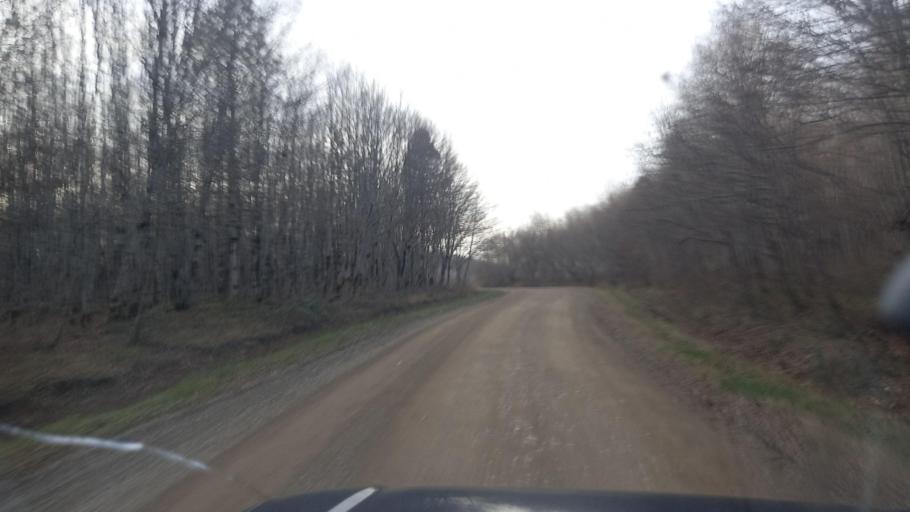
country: RU
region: Krasnodarskiy
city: Khadyzhensk
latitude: 44.3359
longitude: 39.2743
